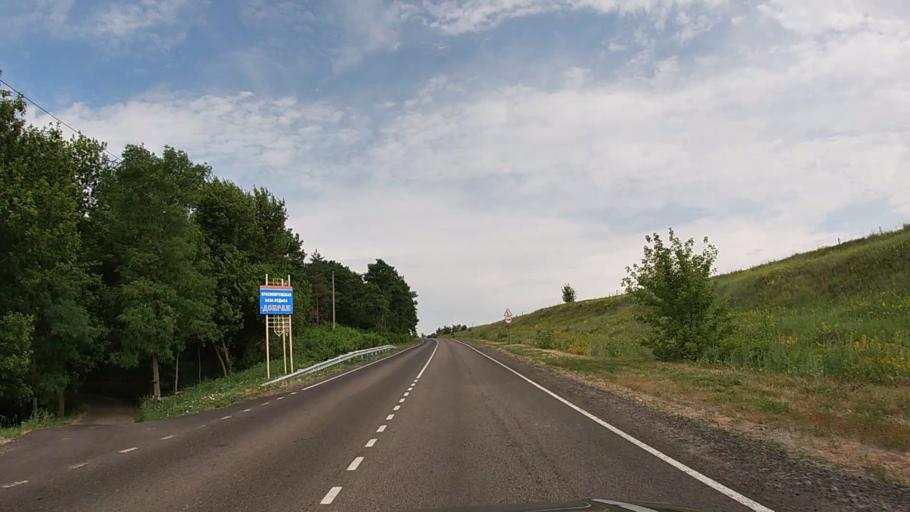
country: RU
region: Belgorod
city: Krasnaya Yaruga
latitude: 50.8285
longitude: 35.4963
